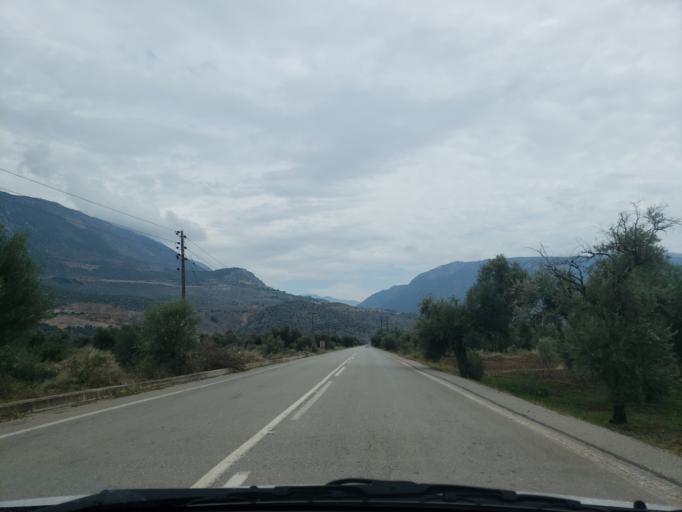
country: GR
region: Central Greece
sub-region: Nomos Fokidos
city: Kirra
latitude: 38.4805
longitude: 22.4362
